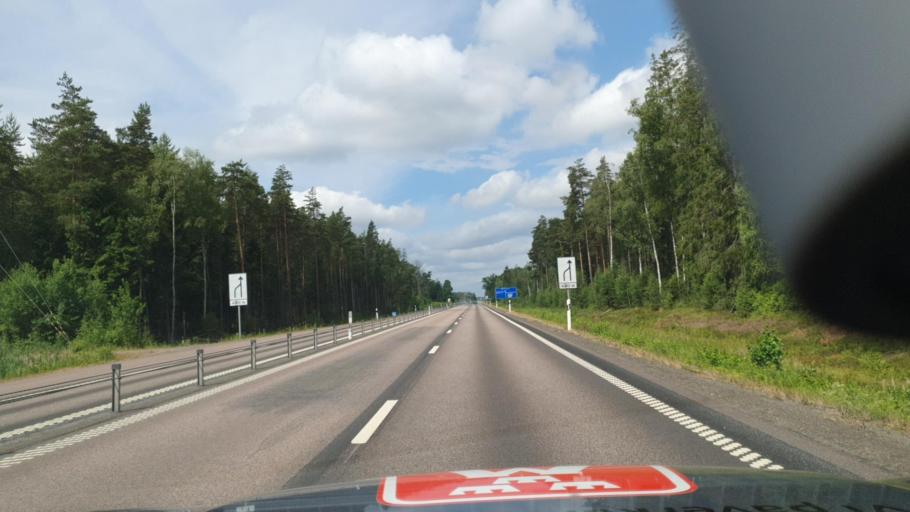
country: SE
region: Kalmar
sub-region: Emmaboda Kommun
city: Emmaboda
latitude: 56.7235
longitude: 15.5924
